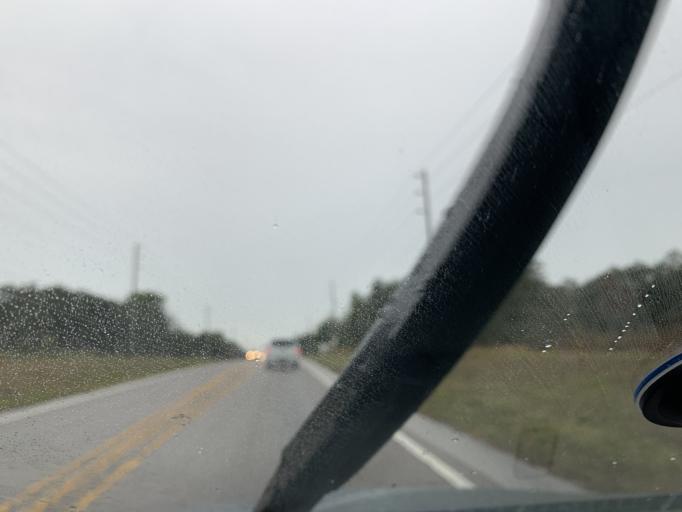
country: US
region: Florida
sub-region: Pasco County
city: Shady Hills
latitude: 28.4337
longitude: -82.5154
